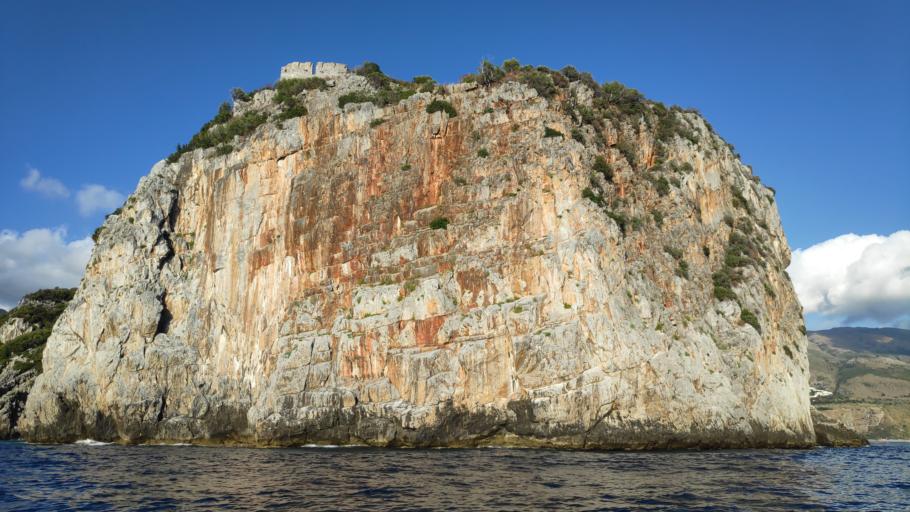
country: IT
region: Calabria
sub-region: Provincia di Cosenza
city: Praia a Mare
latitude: 39.8719
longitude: 15.7680
